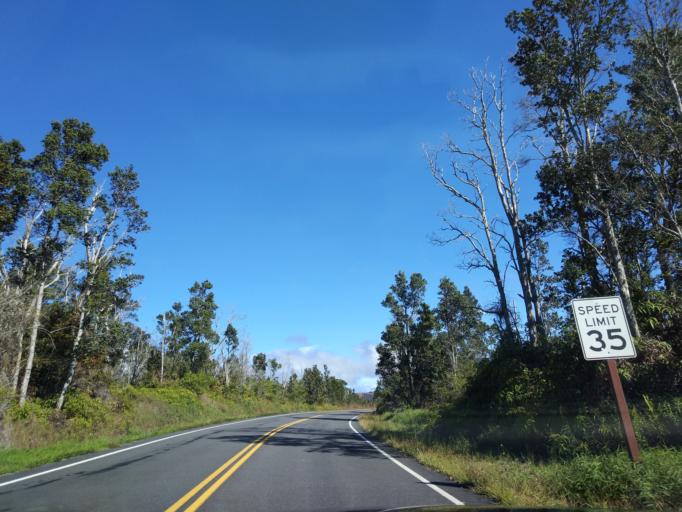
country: US
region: Hawaii
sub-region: Hawaii County
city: Volcano
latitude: 19.3715
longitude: -155.2273
